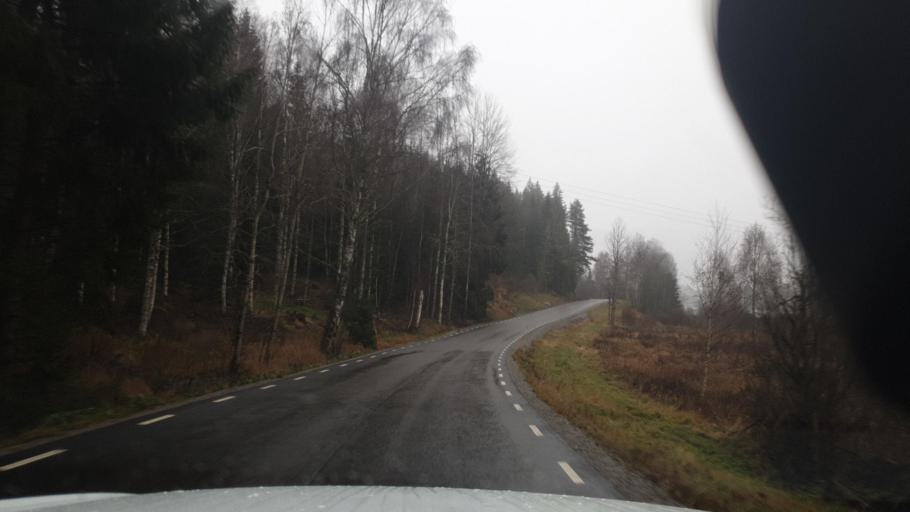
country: SE
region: Vaermland
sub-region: Arvika Kommun
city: Arvika
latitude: 59.6610
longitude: 12.7980
